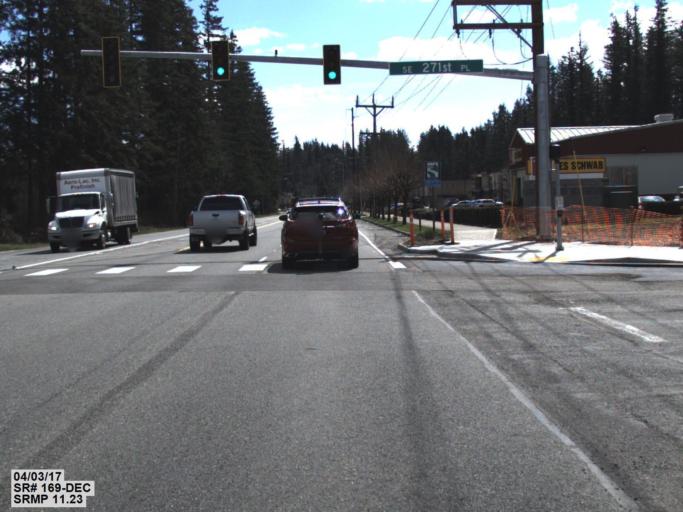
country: US
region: Washington
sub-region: King County
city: Ravensdale
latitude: 47.3584
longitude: -122.0203
